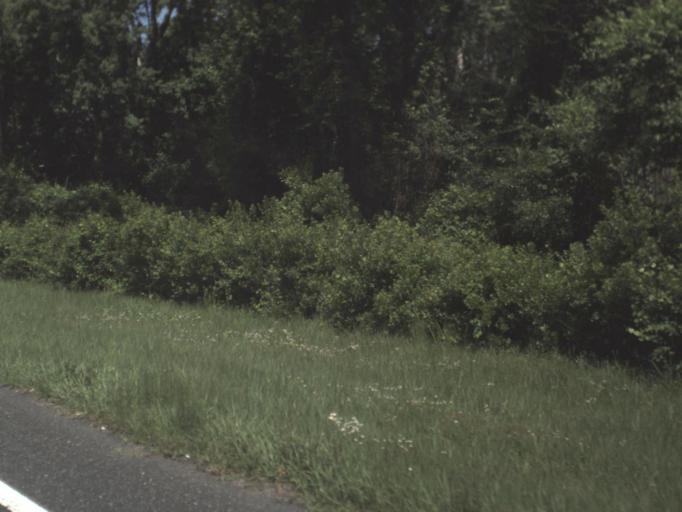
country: US
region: Florida
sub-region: Union County
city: Lake Butler
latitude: 30.2075
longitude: -82.4044
